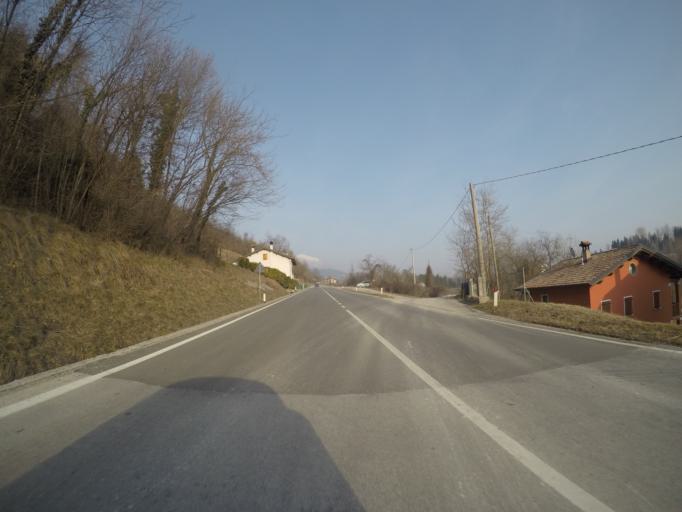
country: IT
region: Veneto
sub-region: Provincia di Belluno
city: Sospirolo
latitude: 46.1500
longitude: 12.1110
